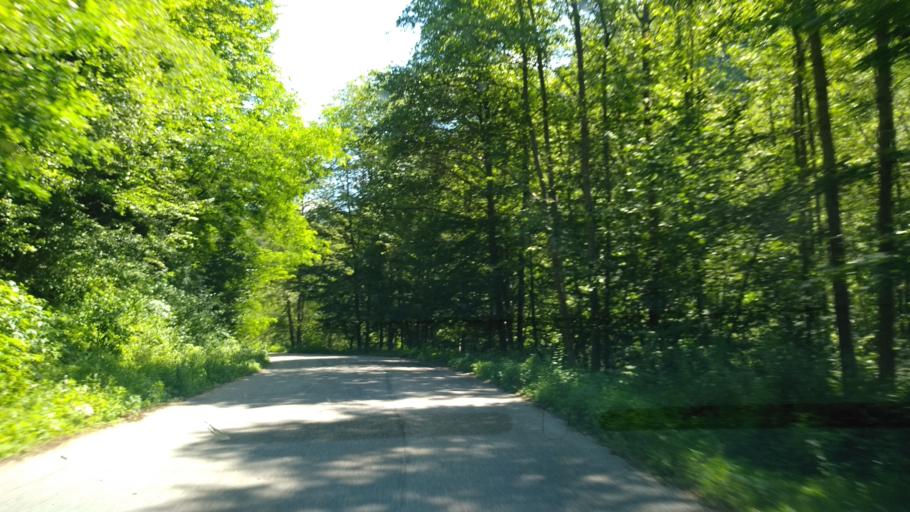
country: RO
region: Hunedoara
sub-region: Comuna Orastioara de Sus
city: Orastioara de Sus
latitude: 45.6369
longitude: 23.1993
